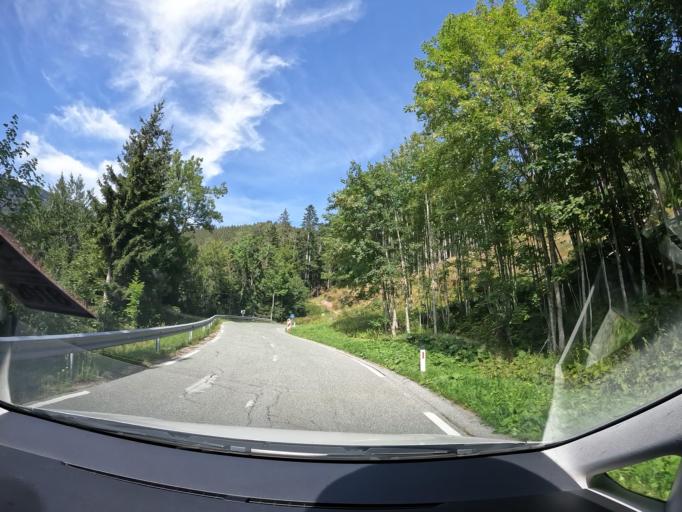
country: AT
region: Carinthia
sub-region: Politischer Bezirk Sankt Veit an der Glan
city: Liebenfels
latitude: 46.7130
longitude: 14.2596
